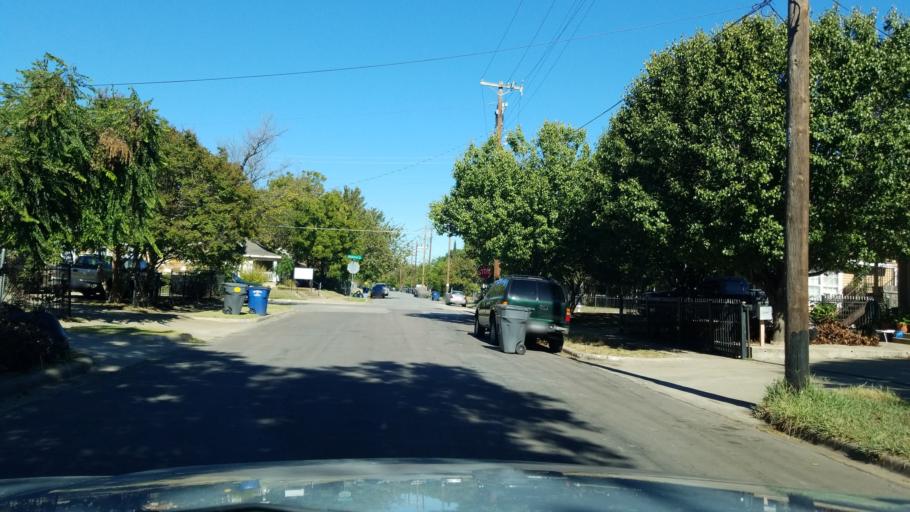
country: US
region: Texas
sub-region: Dallas County
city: Dallas
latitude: 32.7949
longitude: -96.7562
